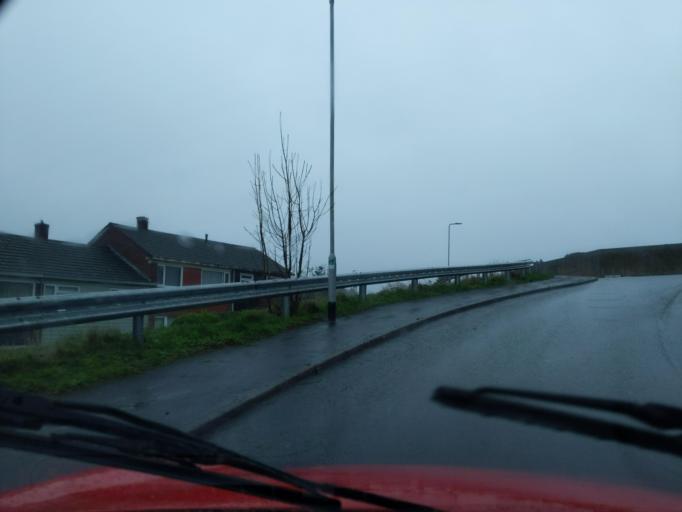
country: GB
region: England
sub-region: Plymouth
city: Plymstock
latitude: 50.4032
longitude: -4.1068
